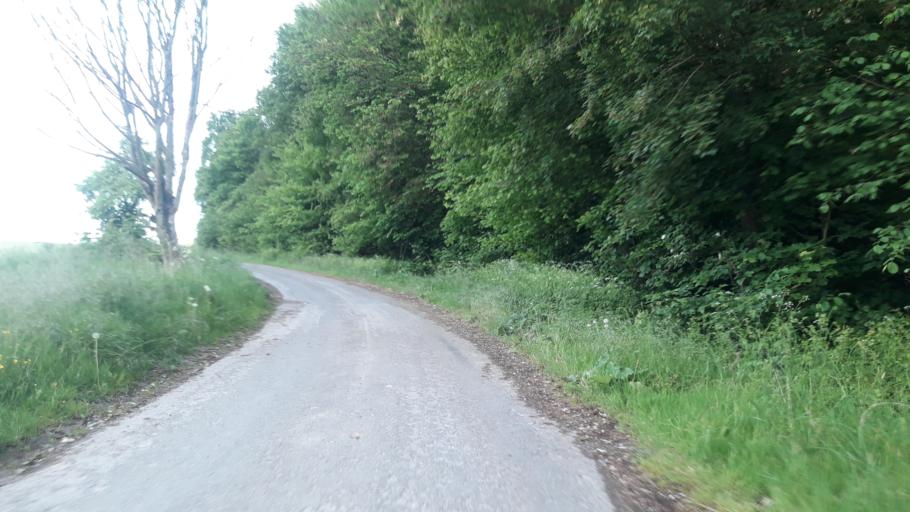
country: DE
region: North Rhine-Westphalia
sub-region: Regierungsbezirk Detmold
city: Paderborn
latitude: 51.6686
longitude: 8.7855
